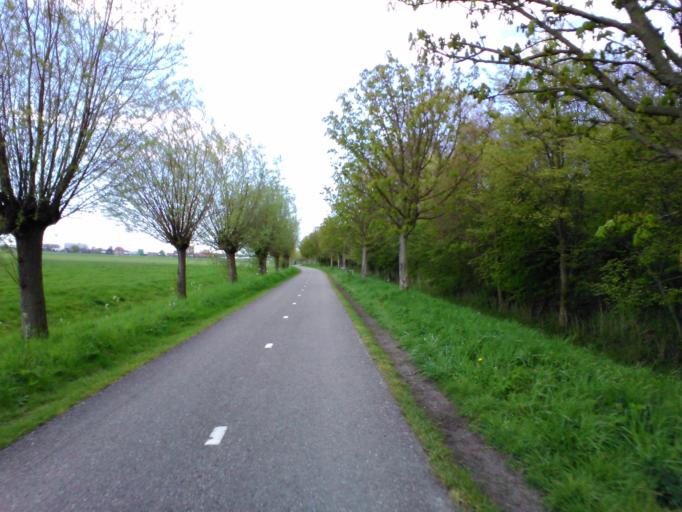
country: NL
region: South Holland
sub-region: Gemeente Westland
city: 's-Gravenzande
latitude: 51.9746
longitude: 4.1674
